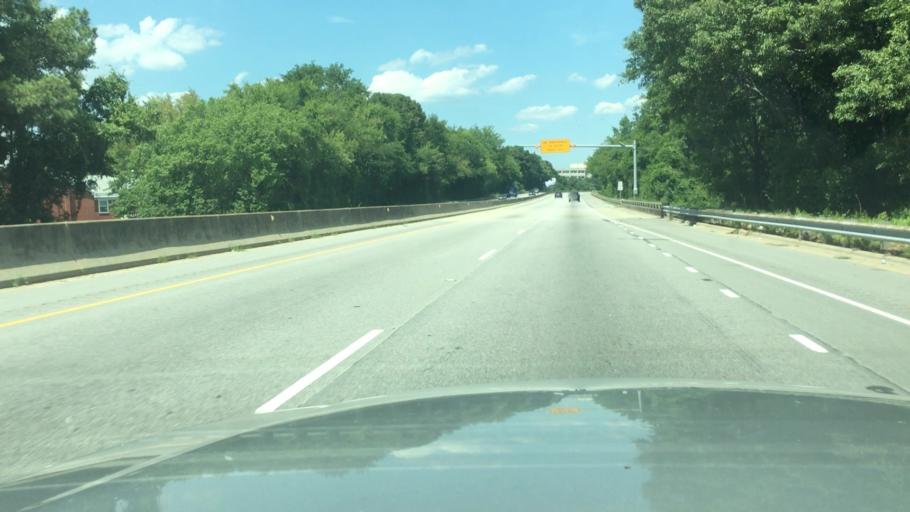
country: US
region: North Carolina
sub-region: Cumberland County
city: Fayetteville
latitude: 35.0662
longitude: -78.8867
